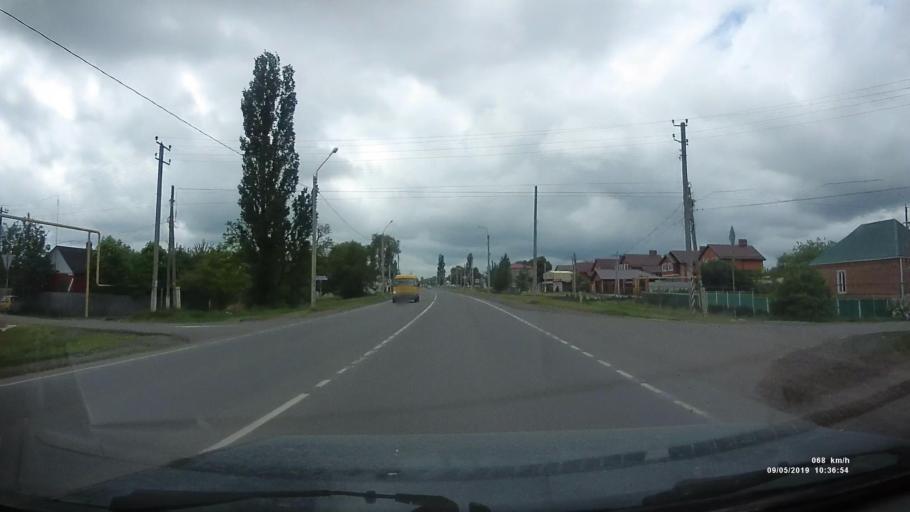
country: RU
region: Rostov
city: Peshkovo
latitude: 47.0249
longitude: 39.4053
